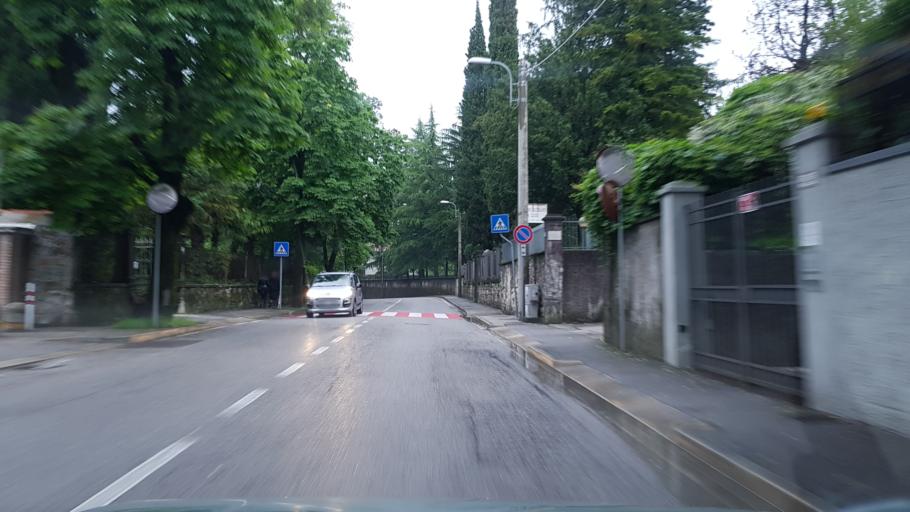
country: IT
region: Friuli Venezia Giulia
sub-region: Provincia di Gorizia
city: Gorizia
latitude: 45.9522
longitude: 13.6202
